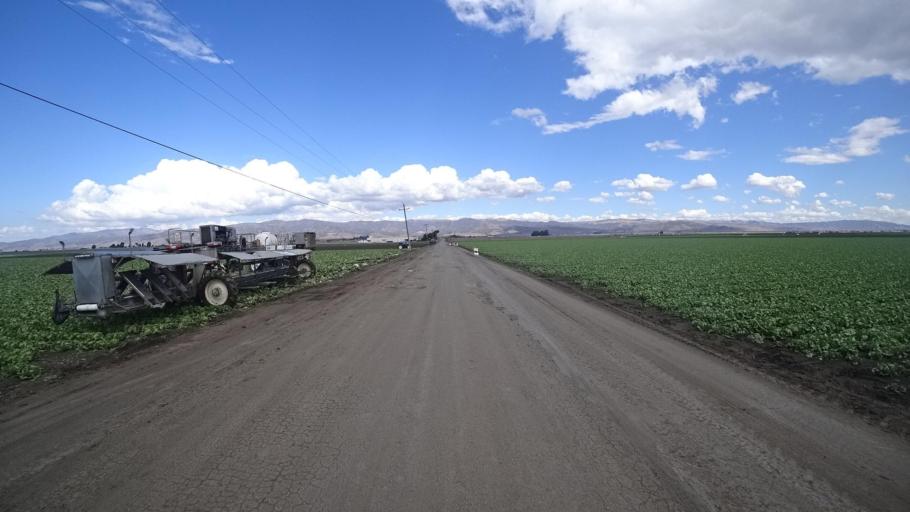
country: US
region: California
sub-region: Monterey County
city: Chualar
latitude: 36.5894
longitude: -121.5583
